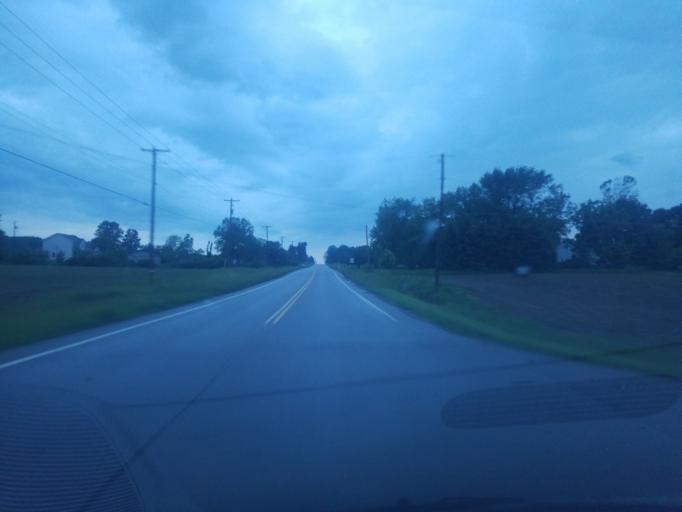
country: US
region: Ohio
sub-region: Mahoning County
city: Canfield
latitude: 40.9882
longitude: -80.7369
